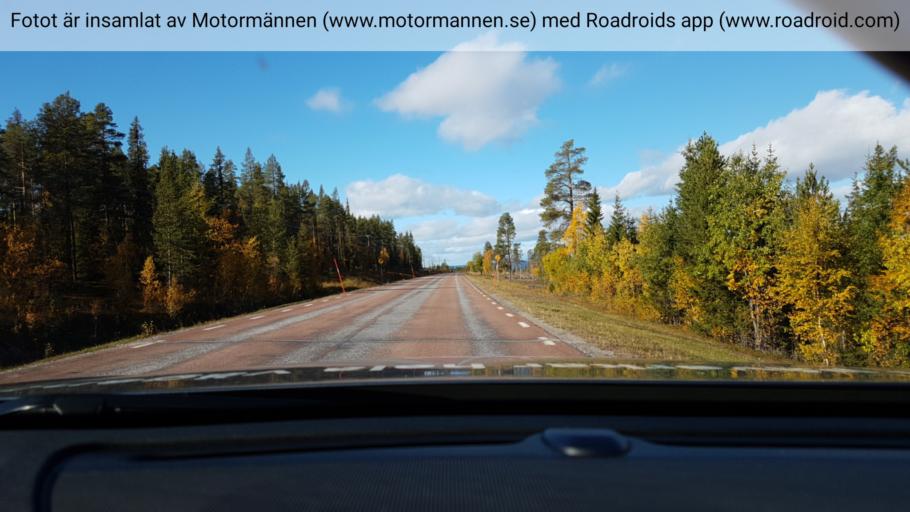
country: SE
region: Norrbotten
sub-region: Arjeplogs Kommun
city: Arjeplog
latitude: 66.0584
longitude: 17.9748
